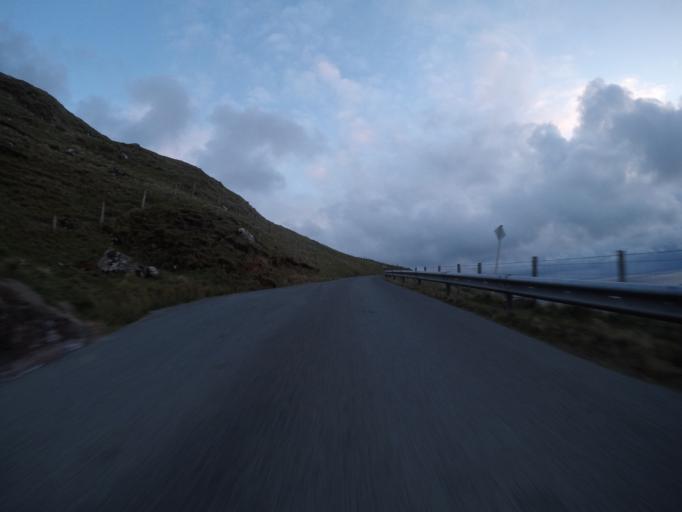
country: GB
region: Scotland
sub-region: Highland
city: Portree
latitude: 57.6641
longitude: -6.3622
